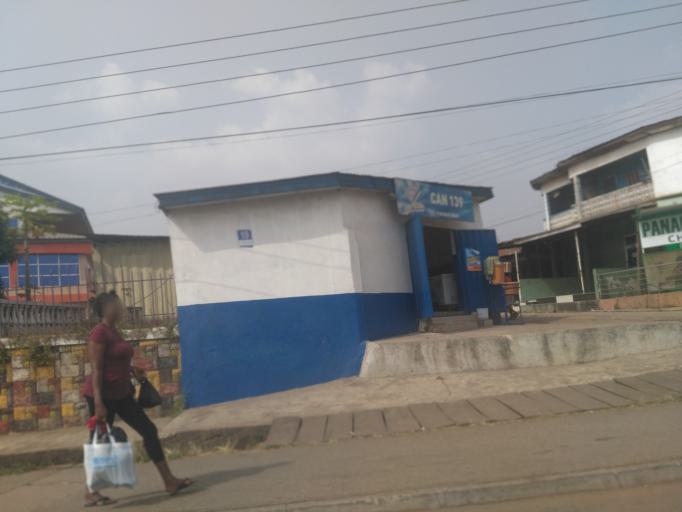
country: GH
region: Ashanti
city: Kumasi
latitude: 6.6892
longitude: -1.6145
